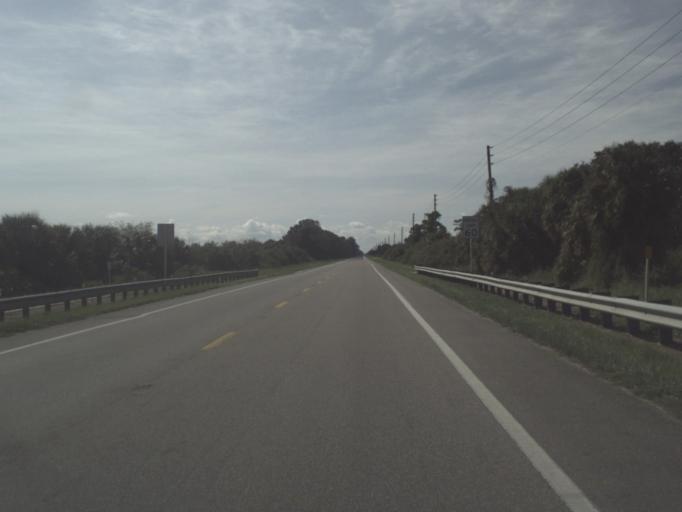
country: US
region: Florida
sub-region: DeSoto County
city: Nocatee
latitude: 27.0091
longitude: -81.7604
